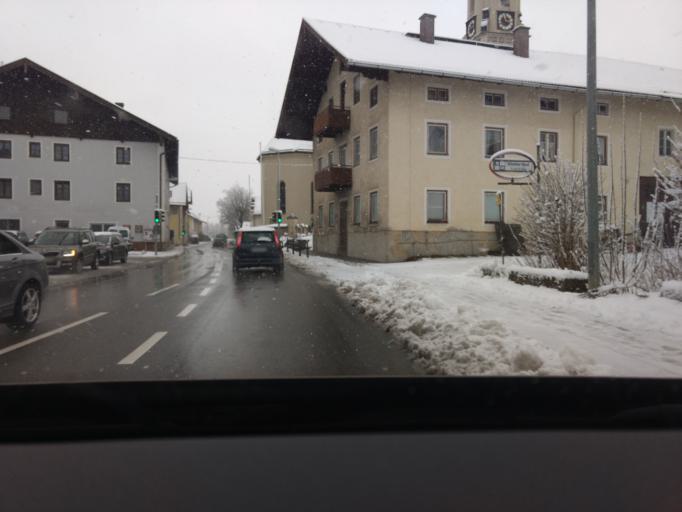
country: DE
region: Bavaria
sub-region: Upper Bavaria
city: Vachendorf
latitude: 47.8612
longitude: 12.6280
